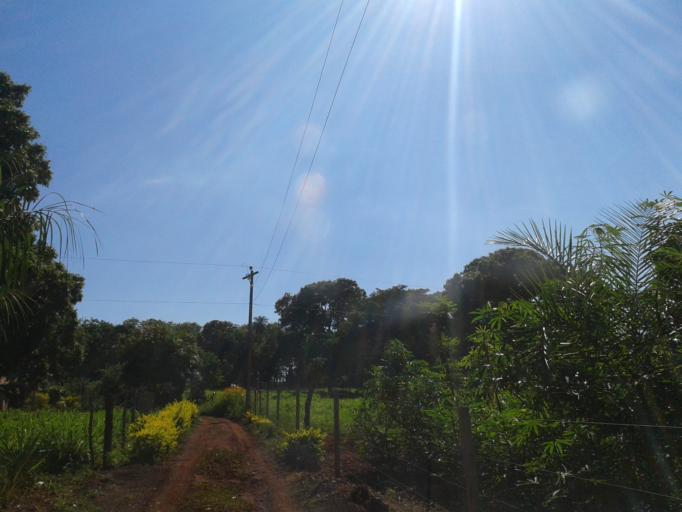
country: BR
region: Minas Gerais
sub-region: Centralina
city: Centralina
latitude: -18.6258
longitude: -49.2949
